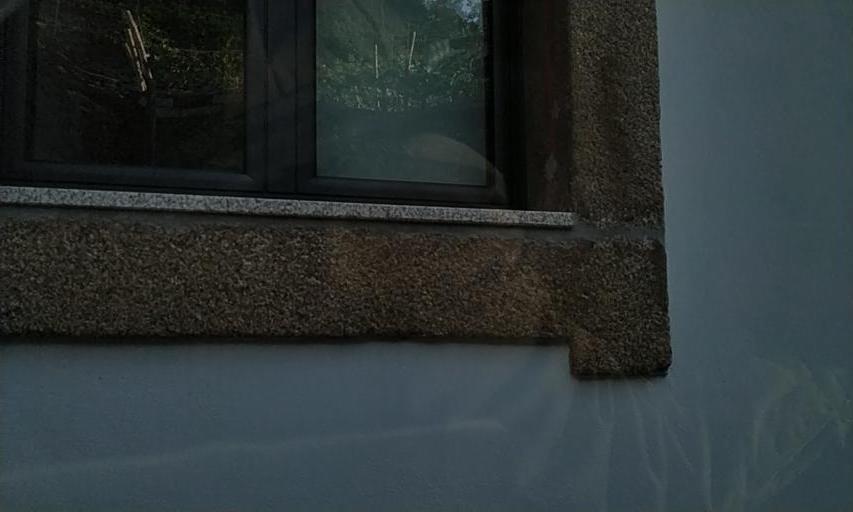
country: PT
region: Vila Real
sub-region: Sabrosa
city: Vilela
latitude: 41.2065
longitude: -7.5497
